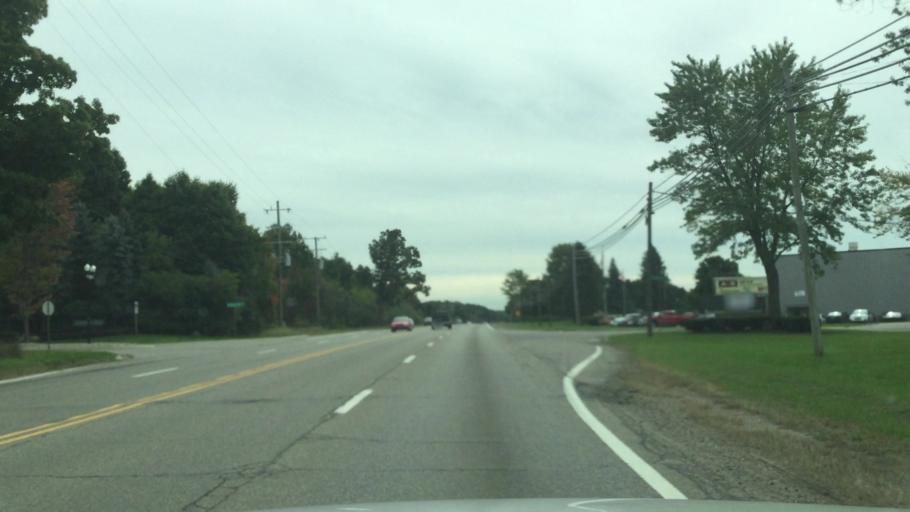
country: US
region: Michigan
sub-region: Oakland County
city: Clarkston
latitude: 42.7770
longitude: -83.4958
